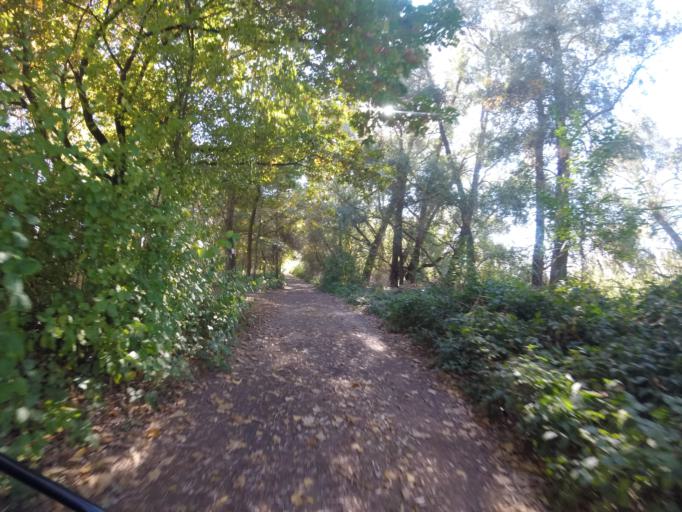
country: DE
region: Rheinland-Pfalz
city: Otterstadt
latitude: 49.3800
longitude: 8.4598
